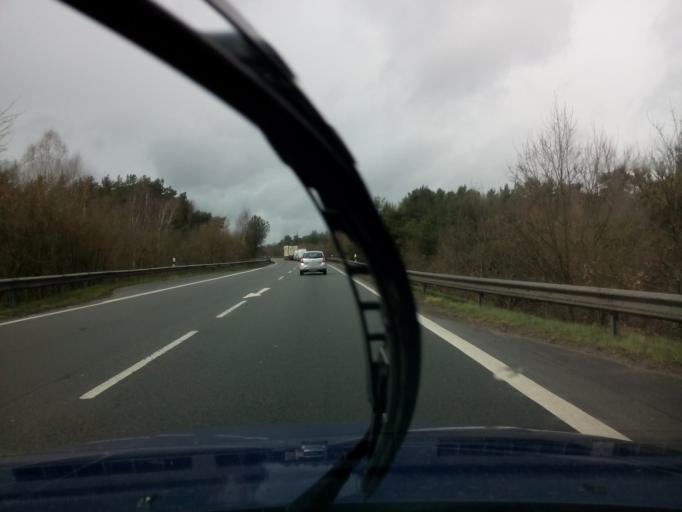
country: DE
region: Lower Saxony
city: Meppen
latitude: 52.7074
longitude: 7.3141
